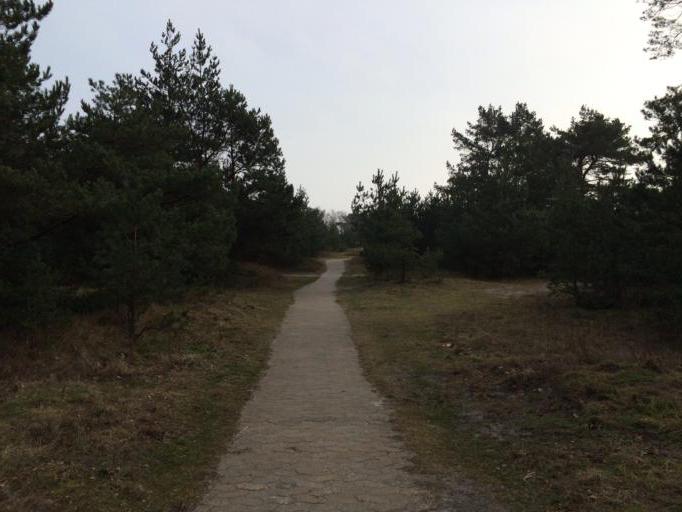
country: SE
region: Skane
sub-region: Vellinge Kommun
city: Skanor med Falsterbo
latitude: 55.3925
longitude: 12.8481
